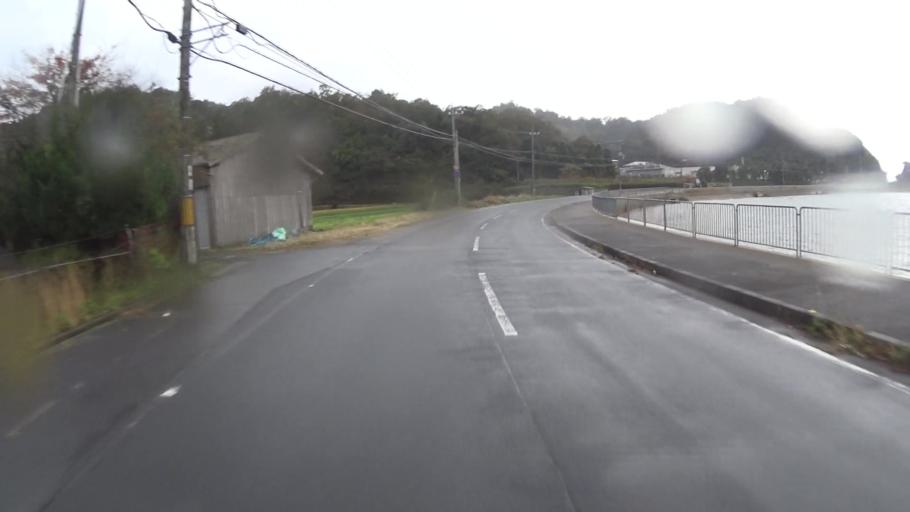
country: JP
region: Kyoto
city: Miyazu
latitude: 35.5633
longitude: 135.2133
